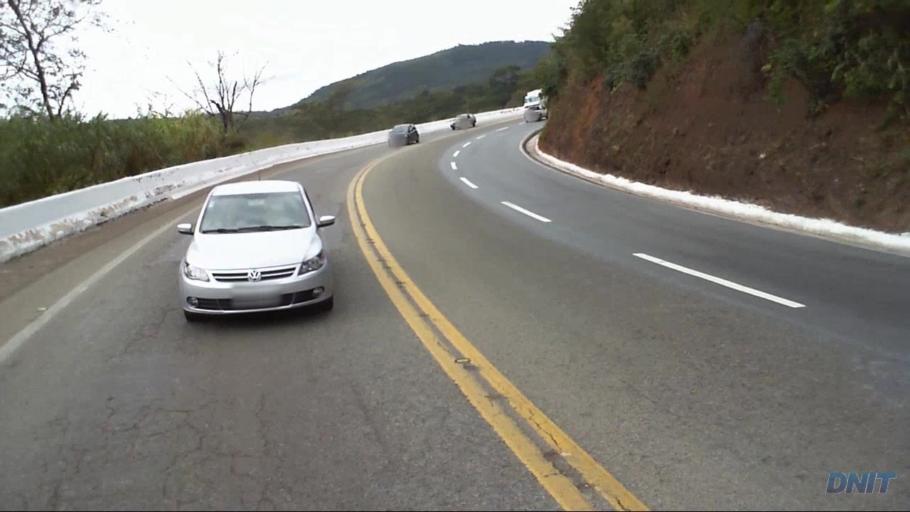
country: BR
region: Minas Gerais
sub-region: Caete
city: Caete
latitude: -19.7863
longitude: -43.7340
